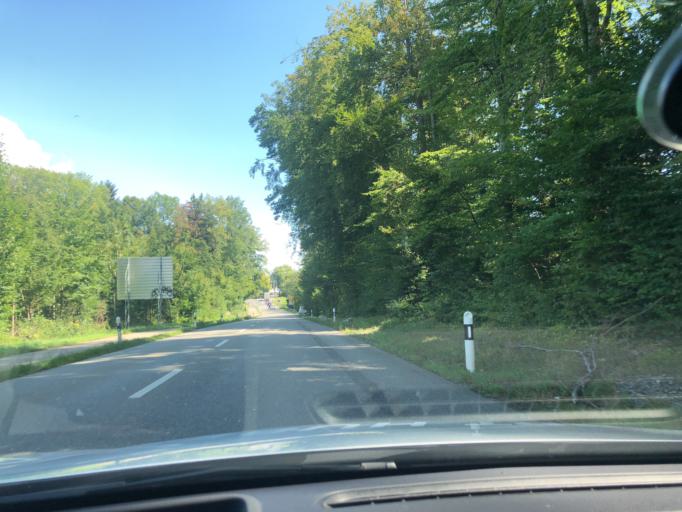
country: CH
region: Thurgau
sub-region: Kreuzlingen District
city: Tagerwilen
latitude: 47.6344
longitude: 9.1533
